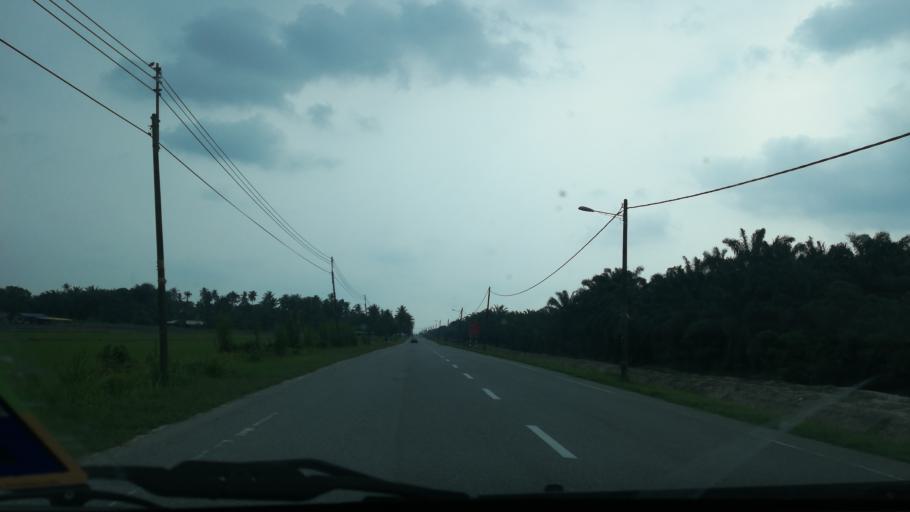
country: MY
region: Perak
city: Teluk Intan
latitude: 4.1170
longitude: 101.0743
